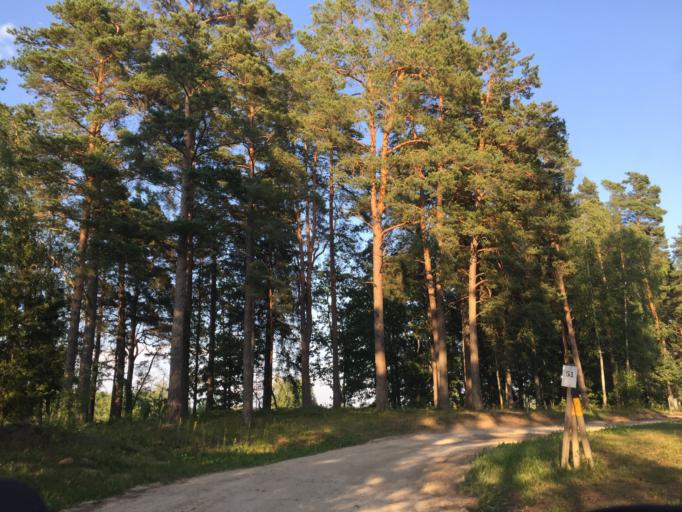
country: LV
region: Riga
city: Bergi
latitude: 56.9797
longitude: 24.3768
